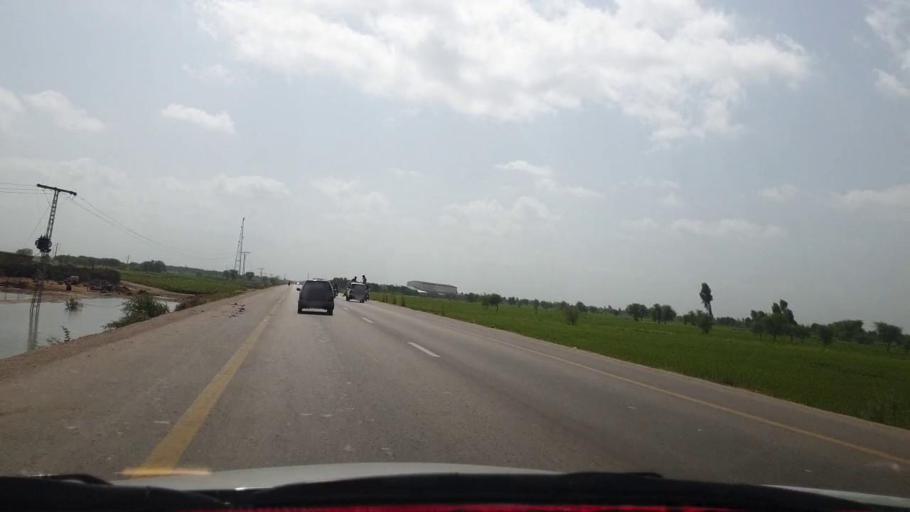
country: PK
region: Sindh
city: Matli
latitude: 24.9398
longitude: 68.7047
